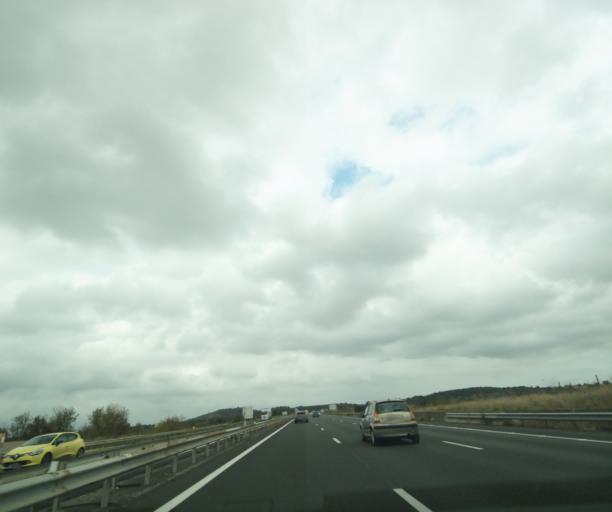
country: FR
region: Languedoc-Roussillon
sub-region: Departement de l'Herault
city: Bessan
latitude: 43.3719
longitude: 3.3985
